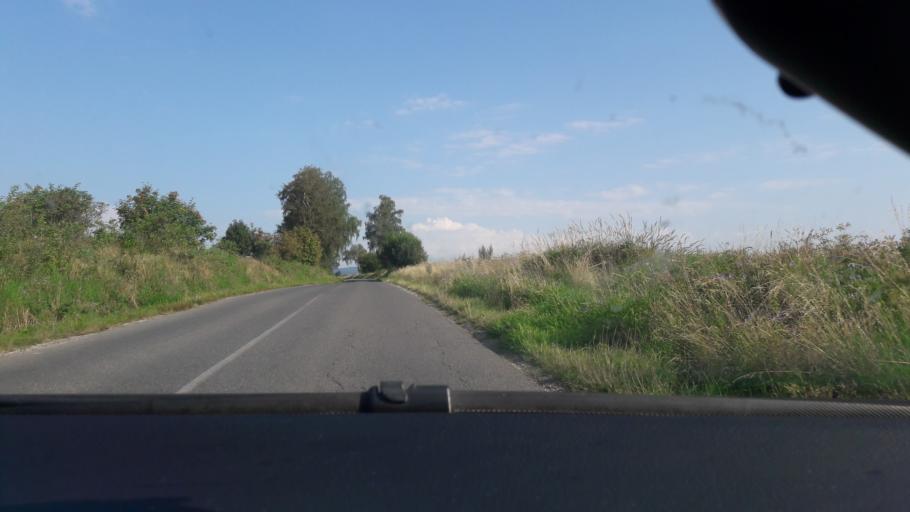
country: SK
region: Presovsky
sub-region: Okres Presov
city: Kezmarok
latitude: 49.1913
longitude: 20.3861
